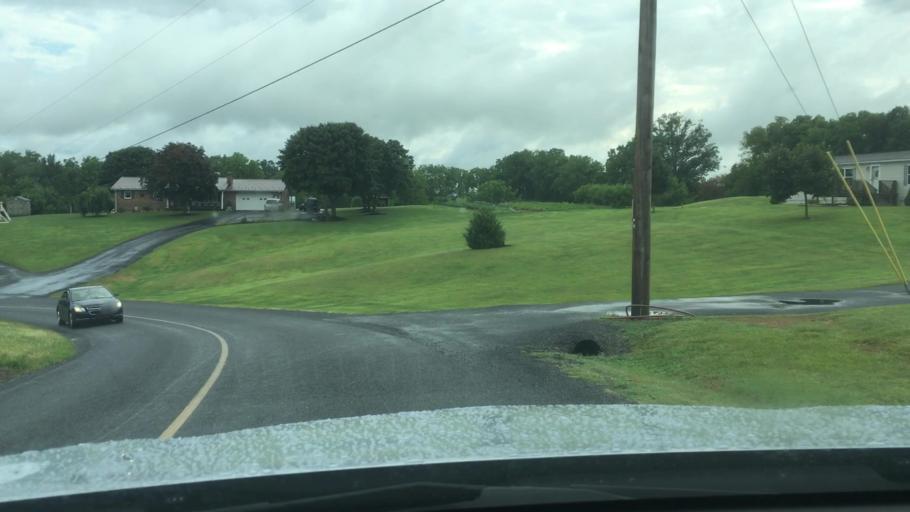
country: US
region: Pennsylvania
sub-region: Franklin County
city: Greencastle
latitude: 39.8712
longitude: -77.7911
